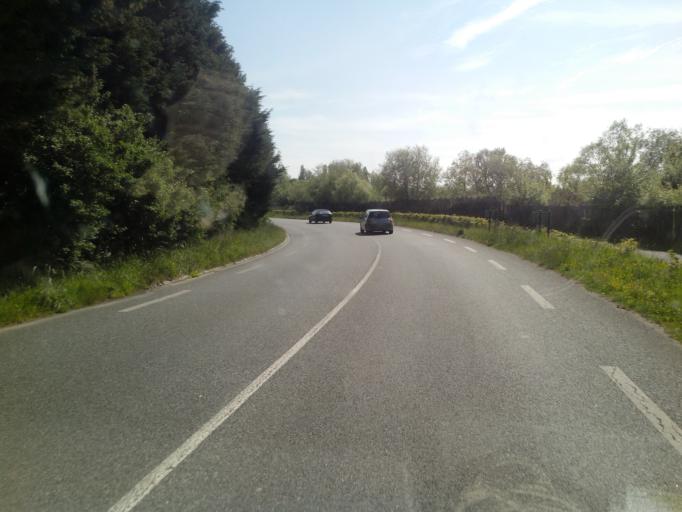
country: FR
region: Nord-Pas-de-Calais
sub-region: Departement du Pas-de-Calais
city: Verton
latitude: 50.3638
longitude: 1.6534
